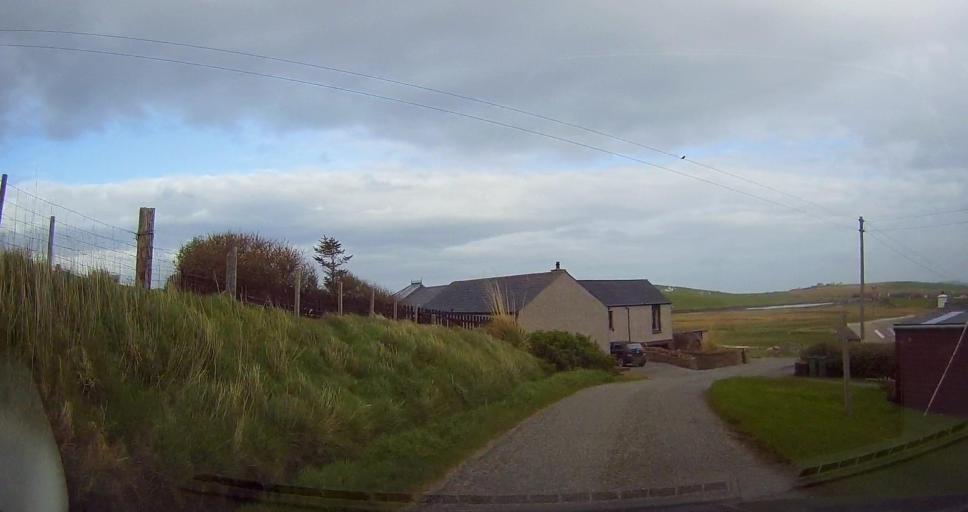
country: GB
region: Scotland
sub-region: Shetland Islands
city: Sandwick
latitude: 60.0481
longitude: -1.2158
